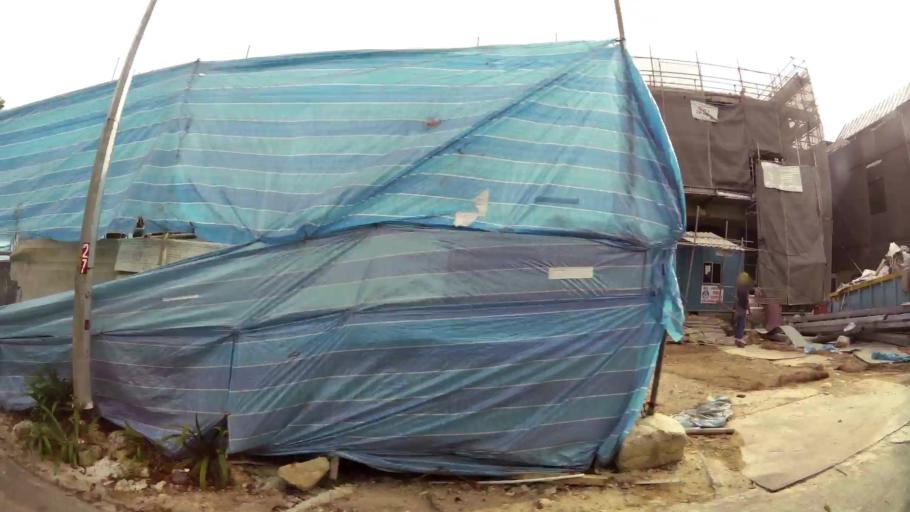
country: SG
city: Singapore
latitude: 1.3261
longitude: 103.8225
